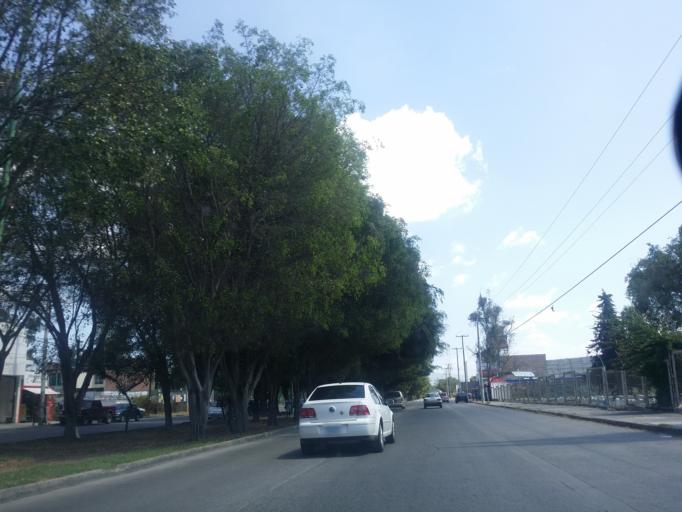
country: MX
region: Guanajuato
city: Leon
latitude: 21.1453
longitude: -101.6636
